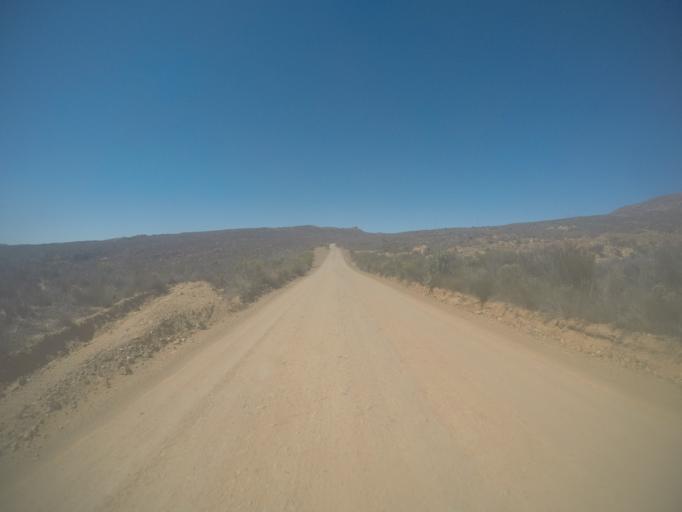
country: ZA
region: Western Cape
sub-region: West Coast District Municipality
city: Clanwilliam
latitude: -32.5027
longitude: 19.2805
